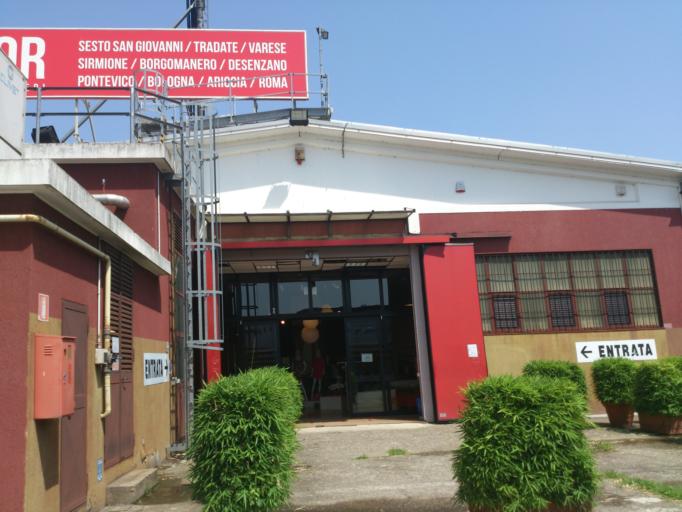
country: IT
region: Lombardy
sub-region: Citta metropolitana di Milano
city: Cologno Monzese
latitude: 45.5265
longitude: 9.2626
